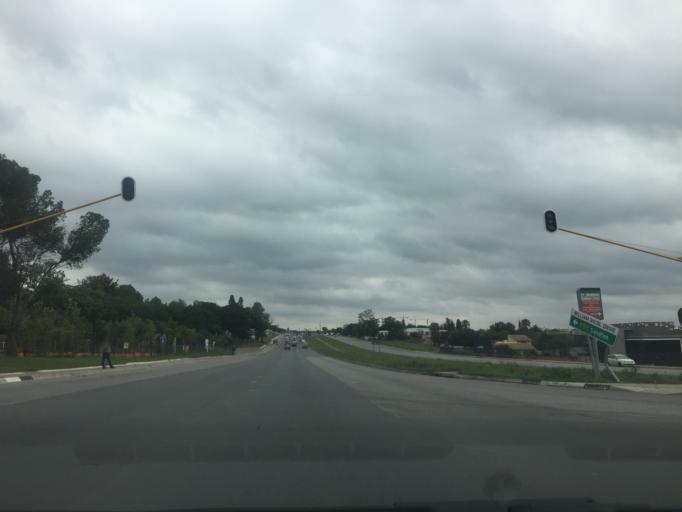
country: ZA
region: Gauteng
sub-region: City of Johannesburg Metropolitan Municipality
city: Diepsloot
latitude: -26.0027
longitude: 28.0133
